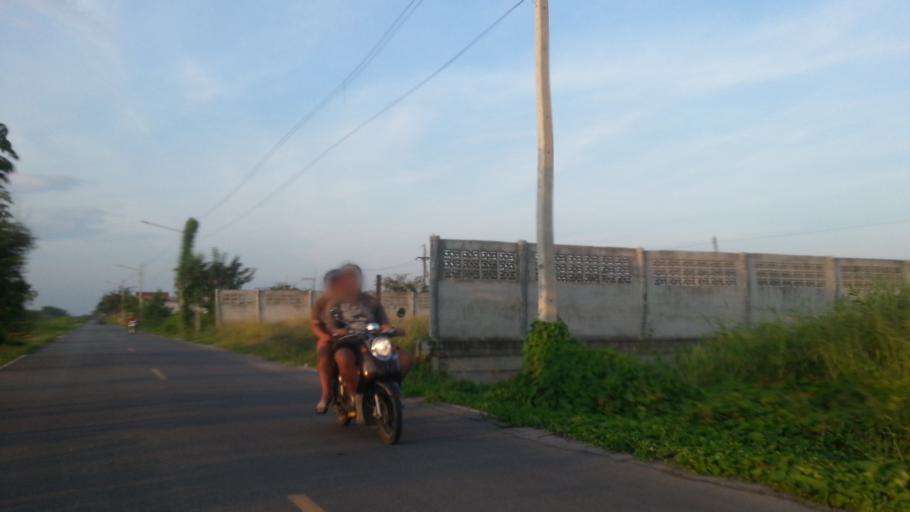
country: TH
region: Pathum Thani
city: Nong Suea
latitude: 14.0479
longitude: 100.8463
